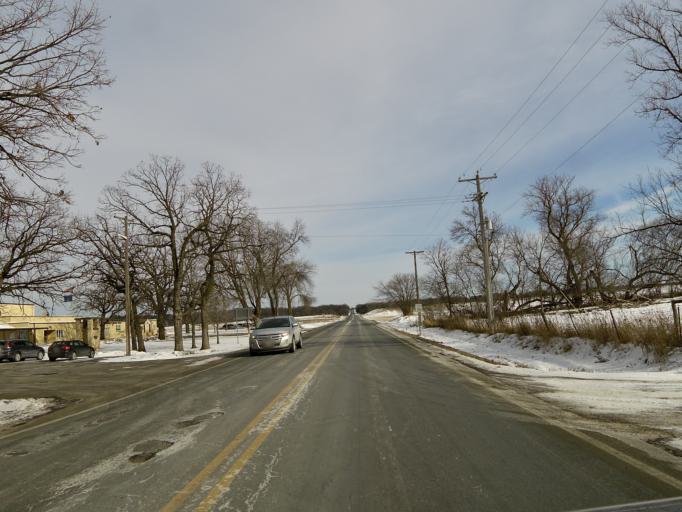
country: US
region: Minnesota
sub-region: Washington County
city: Stillwater
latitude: 45.0607
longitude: -92.7875
